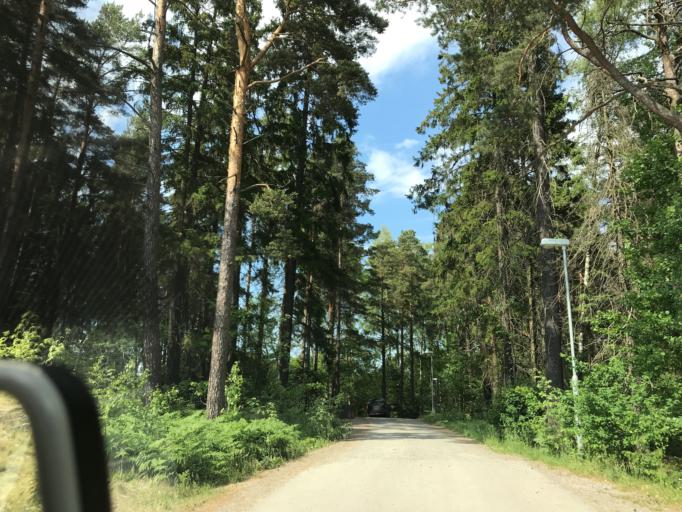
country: SE
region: Stockholm
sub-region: Solna Kommun
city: Rasunda
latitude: 59.4038
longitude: 17.9844
